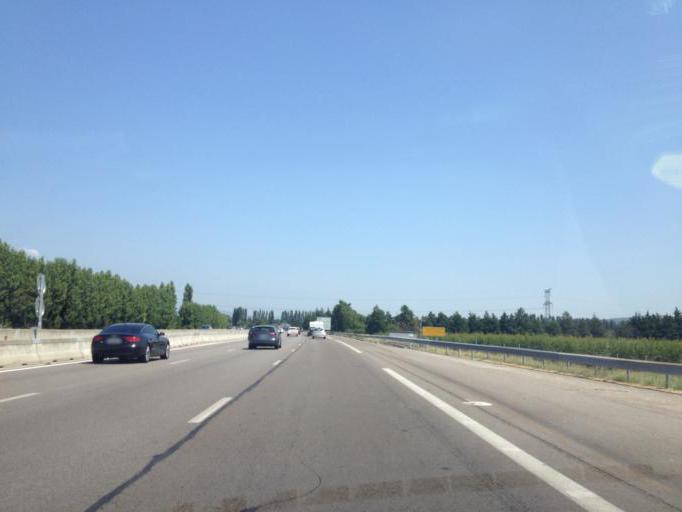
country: FR
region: Rhone-Alpes
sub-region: Departement de la Drome
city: Saulce-sur-Rhone
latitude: 44.6763
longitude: 4.7979
